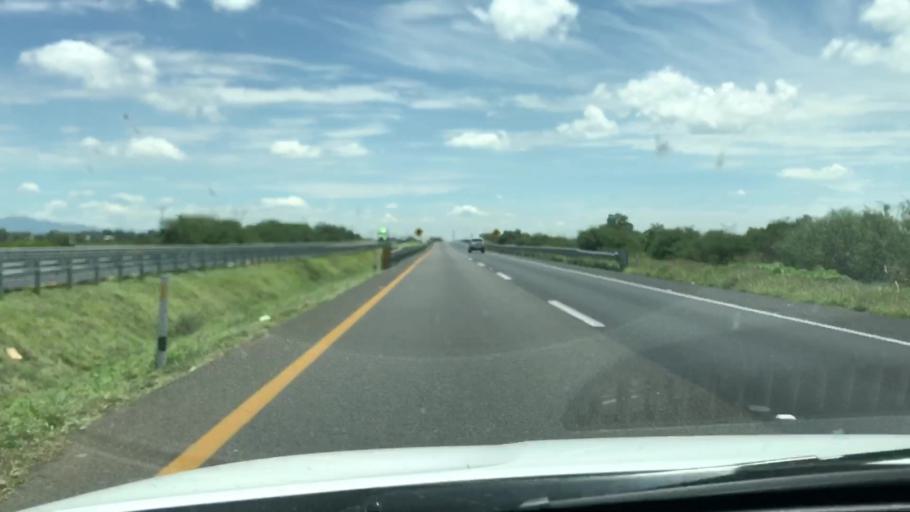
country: MX
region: Guanajuato
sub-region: Villagran
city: Los Angeles
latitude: 20.5785
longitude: -100.9554
